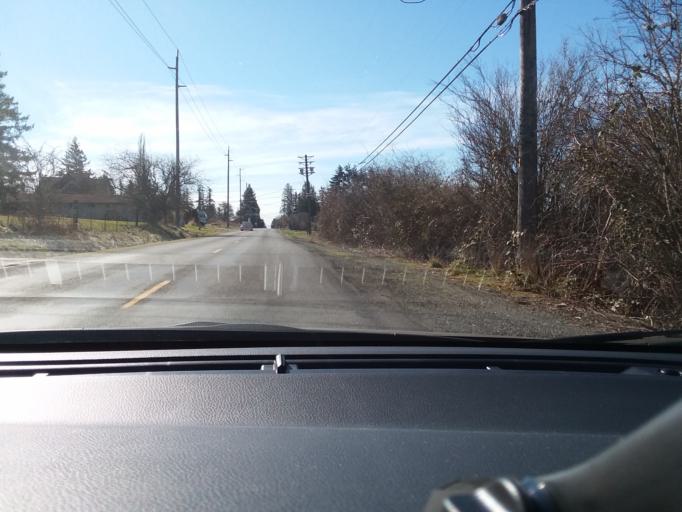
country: US
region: Washington
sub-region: Pierce County
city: Summit
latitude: 47.1723
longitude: -122.3784
